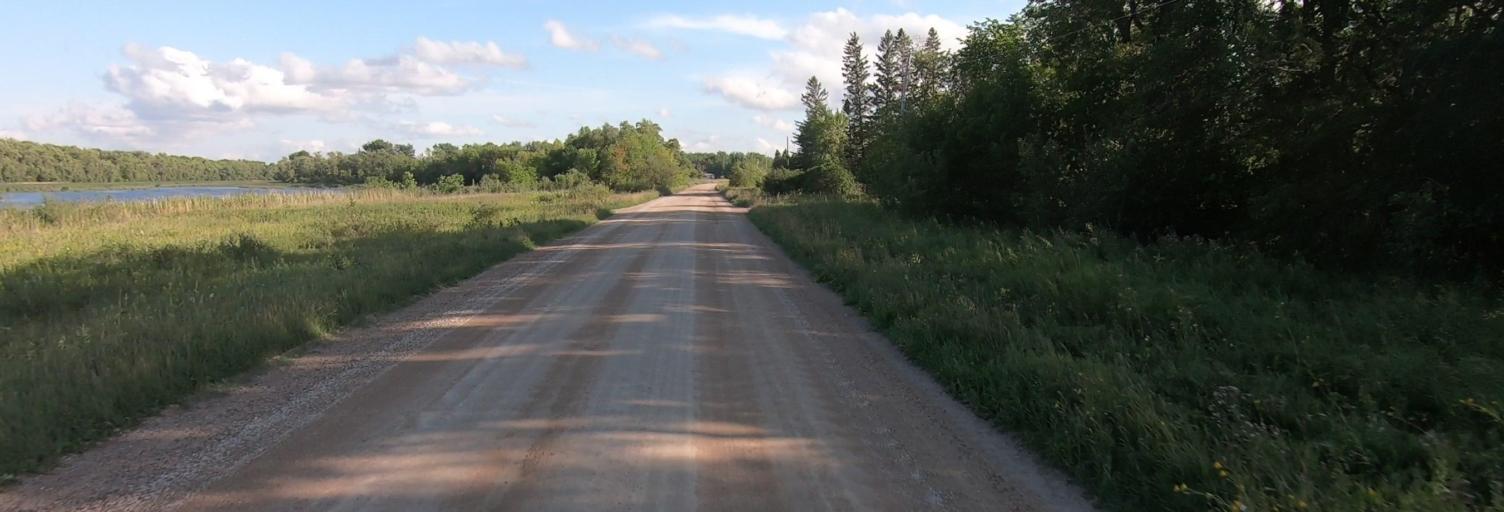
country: CA
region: Manitoba
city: Selkirk
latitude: 50.2466
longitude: -96.8450
